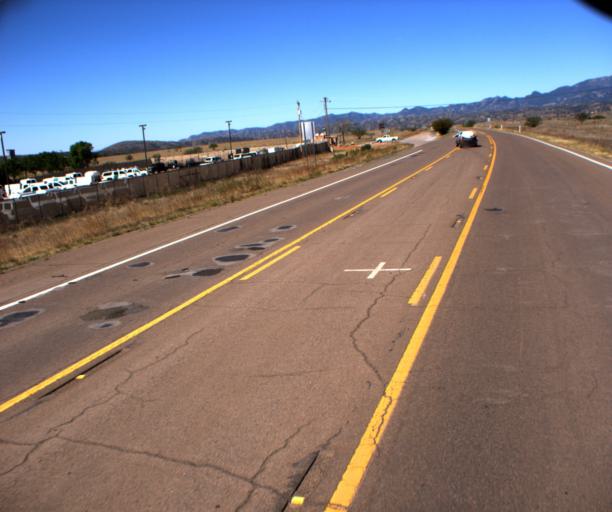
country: US
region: Arizona
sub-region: Pima County
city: Corona de Tucson
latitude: 31.6790
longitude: -110.6586
